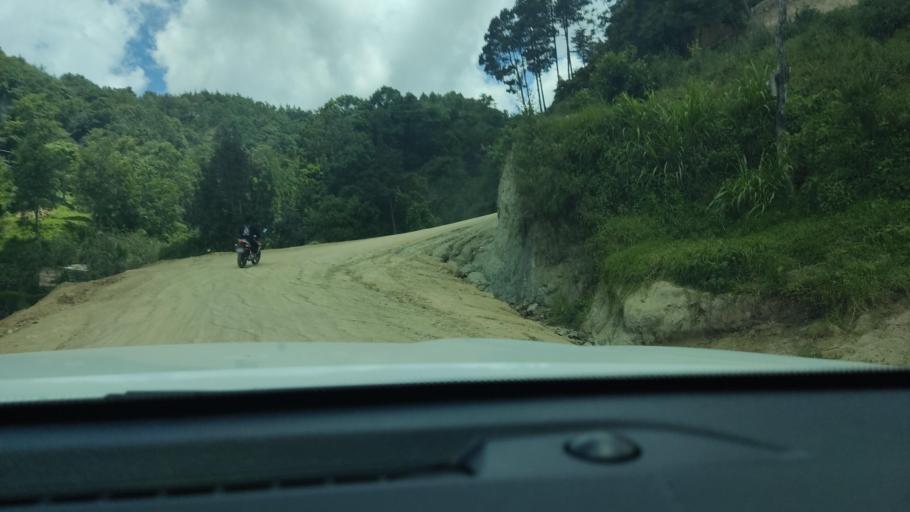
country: GT
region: Chimaltenango
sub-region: Municipio de San Juan Comalapa
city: Comalapa
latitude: 14.7785
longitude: -90.8746
